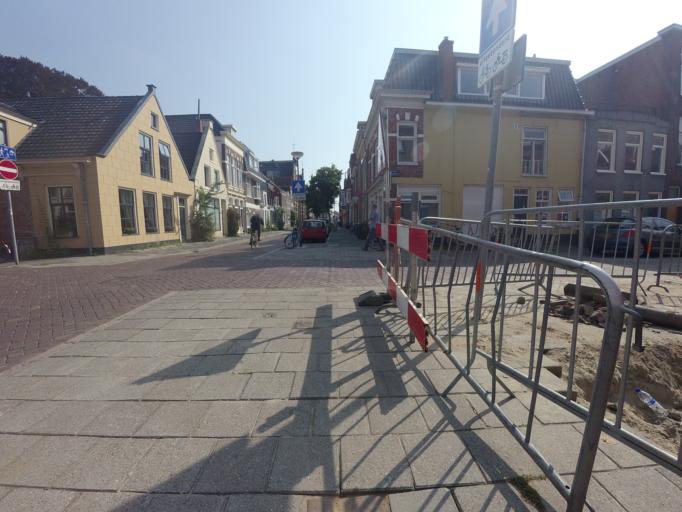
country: NL
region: Groningen
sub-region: Gemeente Groningen
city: Groningen
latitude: 53.2221
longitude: 6.5597
